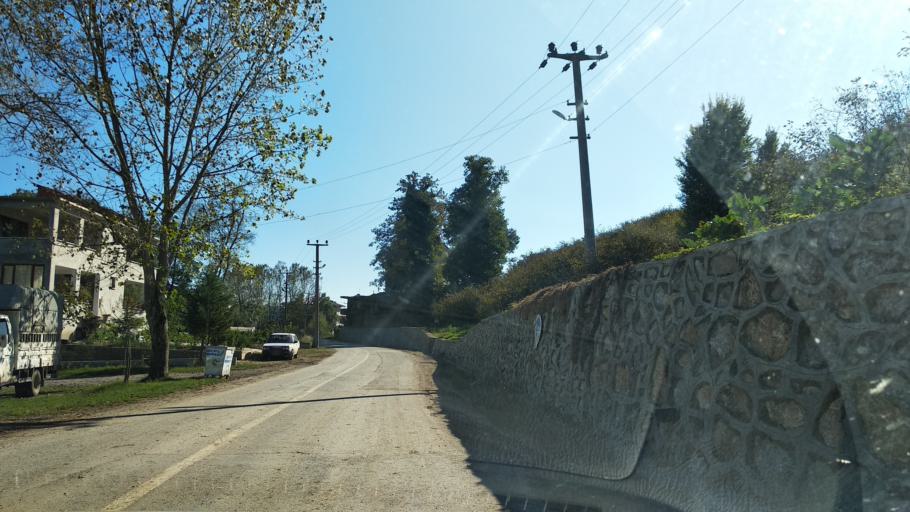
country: TR
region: Sakarya
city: Ortakoy
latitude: 41.0321
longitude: 30.5954
